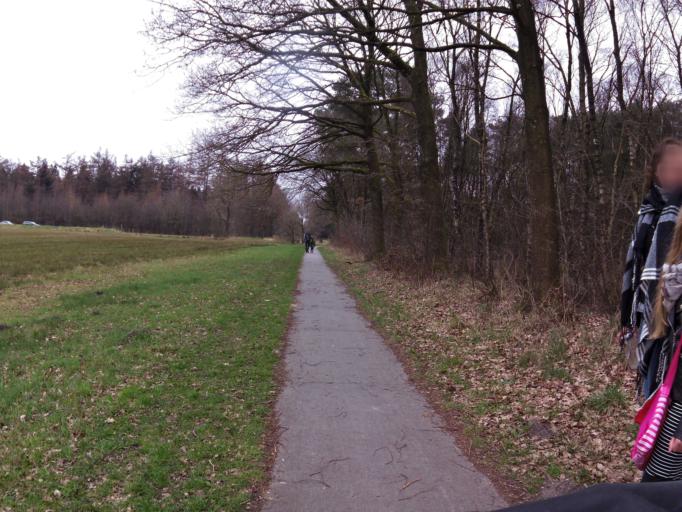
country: NL
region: Drenthe
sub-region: Gemeente Westerveld
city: Dwingeloo
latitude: 52.9794
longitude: 6.3911
